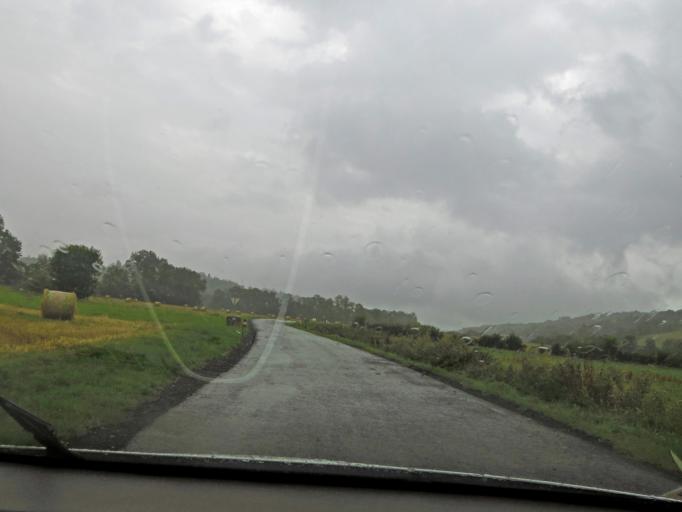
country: FR
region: Auvergne
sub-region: Departement du Puy-de-Dome
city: Saint-Genes-Champanelle
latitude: 45.7047
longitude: 3.0082
